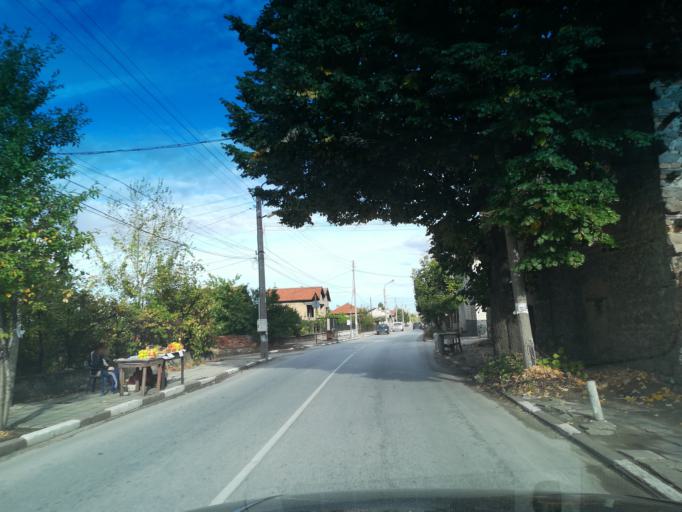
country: BG
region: Pazardzhik
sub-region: Obshtina Bratsigovo
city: Bratsigovo
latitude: 42.0671
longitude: 24.3813
